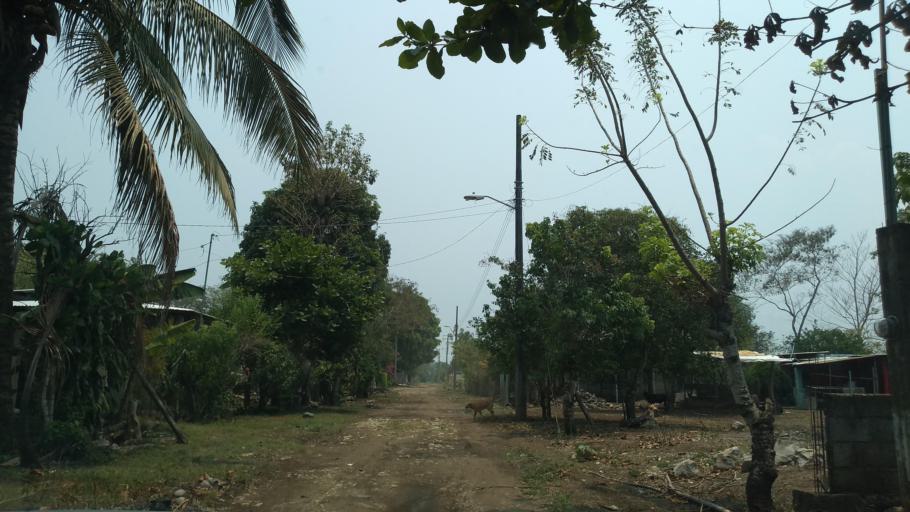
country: MX
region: Veracruz
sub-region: Tezonapa
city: Laguna Chica (Pueblo Nuevo)
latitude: 18.5162
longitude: -96.7382
